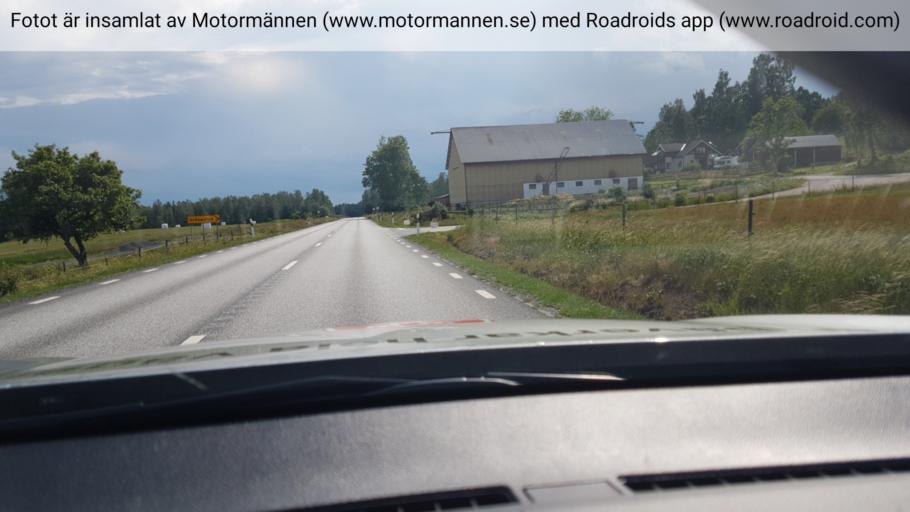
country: SE
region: Joenkoeping
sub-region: Habo Kommun
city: Habo
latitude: 58.0614
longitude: 14.1927
